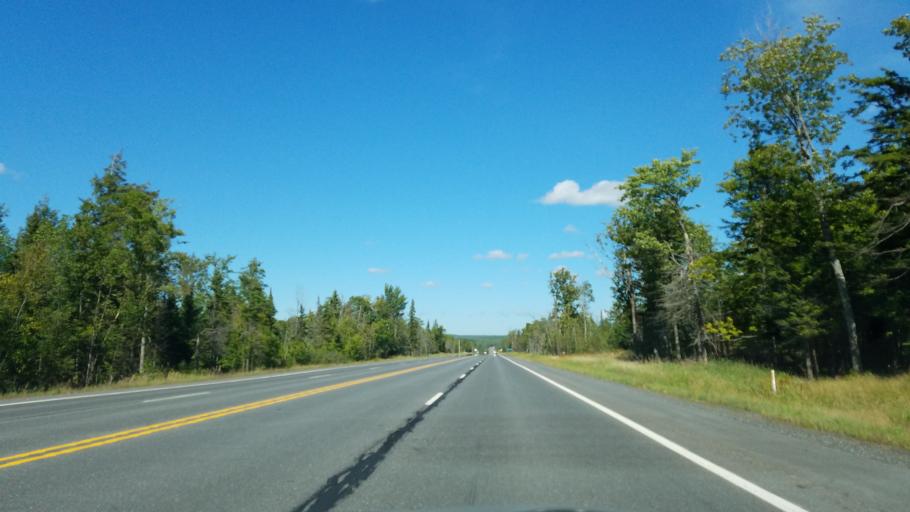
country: US
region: Michigan
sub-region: Baraga County
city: L'Anse
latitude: 46.5603
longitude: -88.5102
